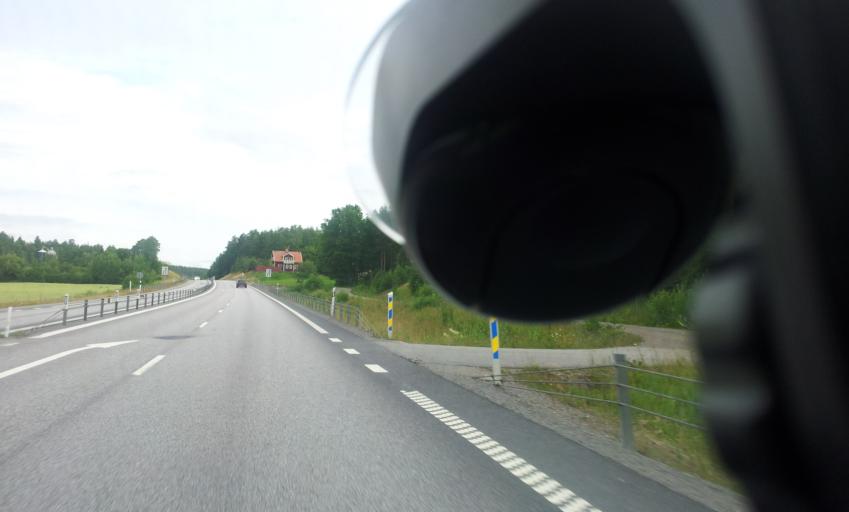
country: SE
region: OEstergoetland
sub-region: Soderkopings Kommun
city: Soederkoeping
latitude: 58.4191
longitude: 16.3963
